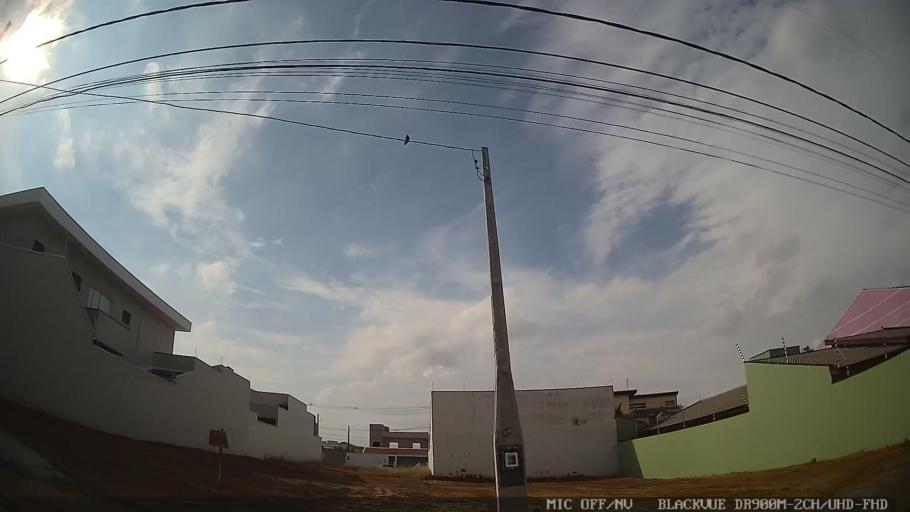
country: BR
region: Sao Paulo
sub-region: Indaiatuba
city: Indaiatuba
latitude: -23.0877
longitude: -47.2277
